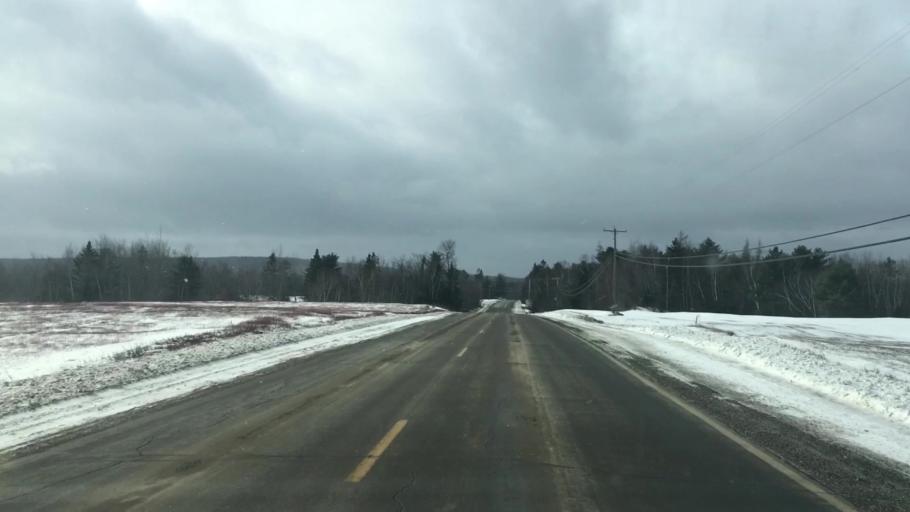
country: US
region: Maine
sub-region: Washington County
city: Calais
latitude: 45.0213
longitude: -67.3799
